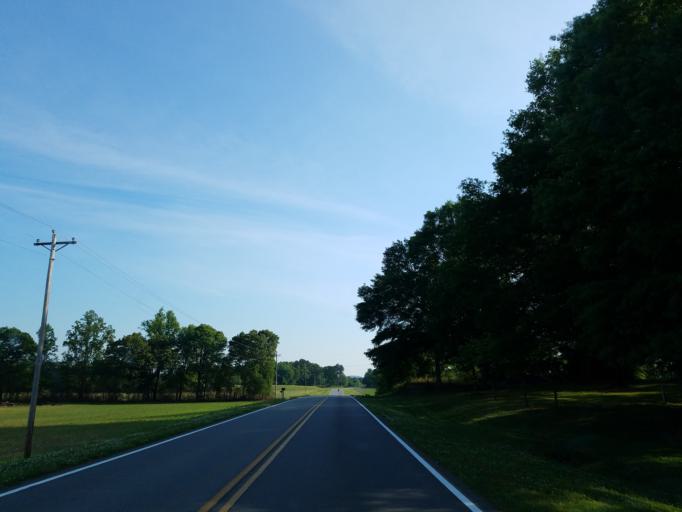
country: US
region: Georgia
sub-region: Chattooga County
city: Trion
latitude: 34.4785
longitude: -85.2616
